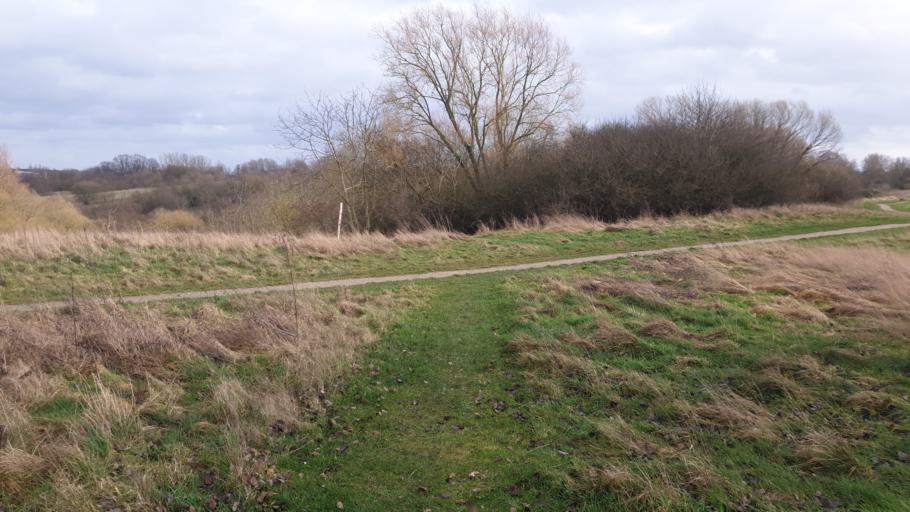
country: DE
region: Mecklenburg-Vorpommern
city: Lankow
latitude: 53.6421
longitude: 11.3640
